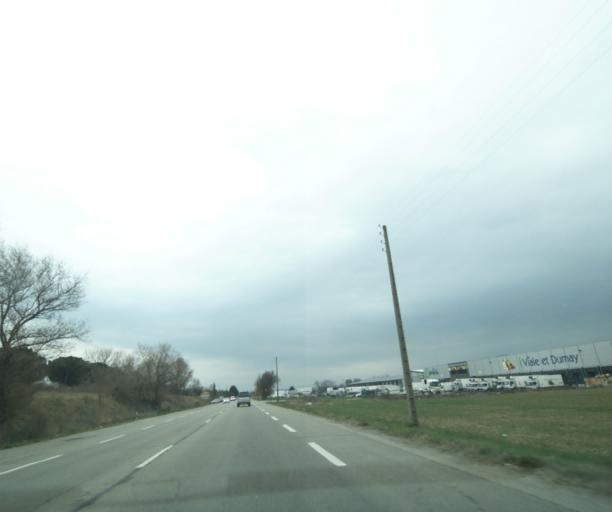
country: FR
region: Rhone-Alpes
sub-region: Departement de l'Ardeche
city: Cornas
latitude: 44.9829
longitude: 4.8811
